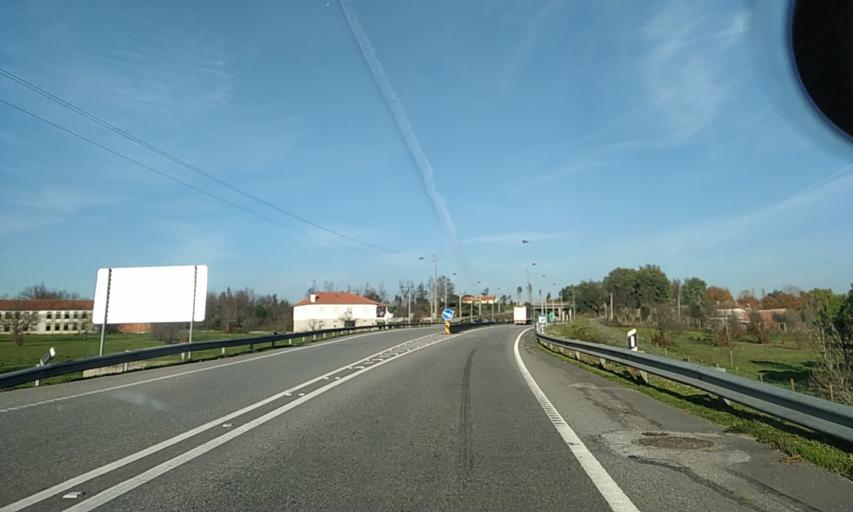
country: PT
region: Viseu
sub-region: Concelho de Tondela
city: Tondela
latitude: 40.5236
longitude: -8.0909
